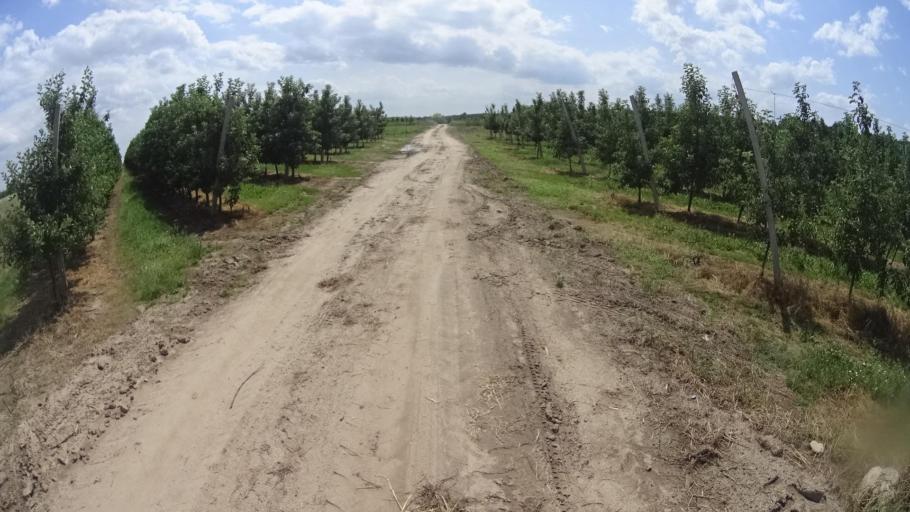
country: PL
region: Masovian Voivodeship
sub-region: Powiat grojecki
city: Goszczyn
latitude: 51.7062
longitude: 20.8282
